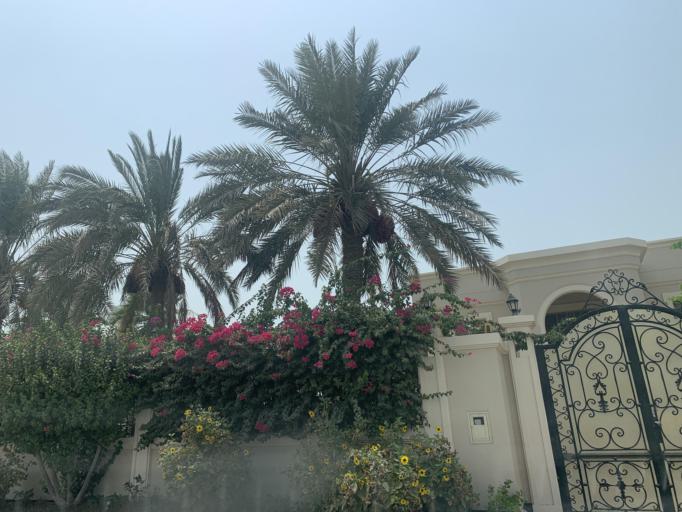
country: BH
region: Northern
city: Madinat `Isa
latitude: 26.1937
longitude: 50.4646
